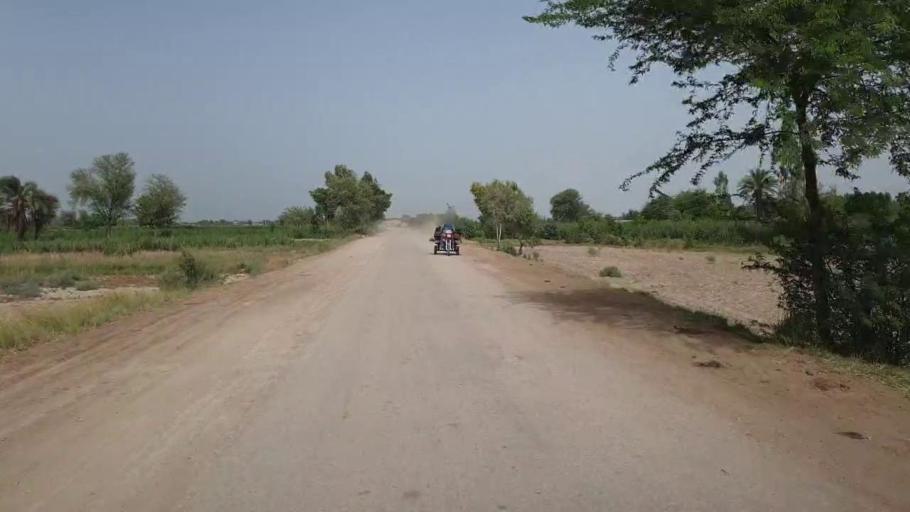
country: PK
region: Sindh
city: Daulatpur
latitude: 26.5482
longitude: 68.0064
